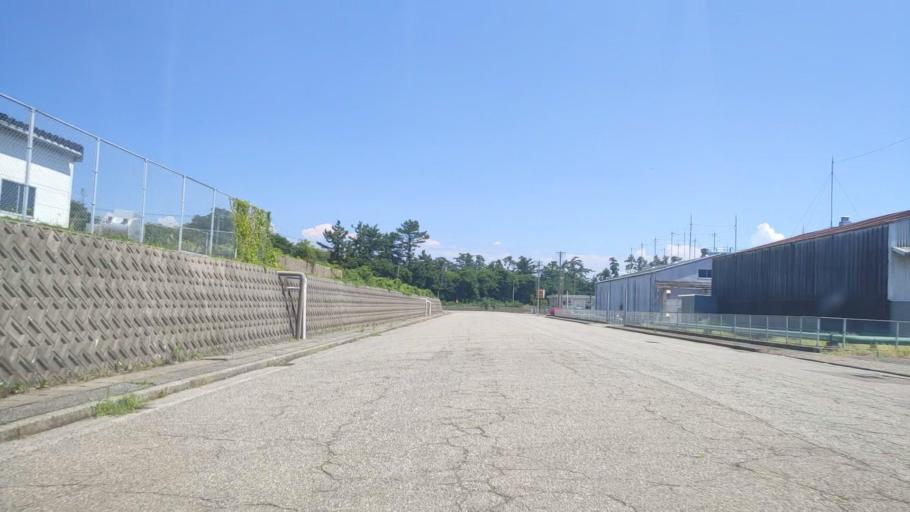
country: JP
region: Ishikawa
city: Kanazawa-shi
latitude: 36.6193
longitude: 136.6130
